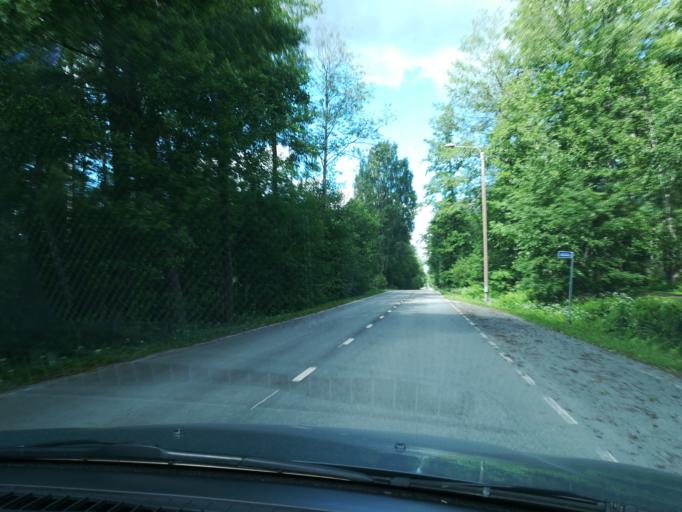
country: FI
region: Southern Savonia
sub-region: Mikkeli
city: Hirvensalmi
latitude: 61.6373
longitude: 26.7807
